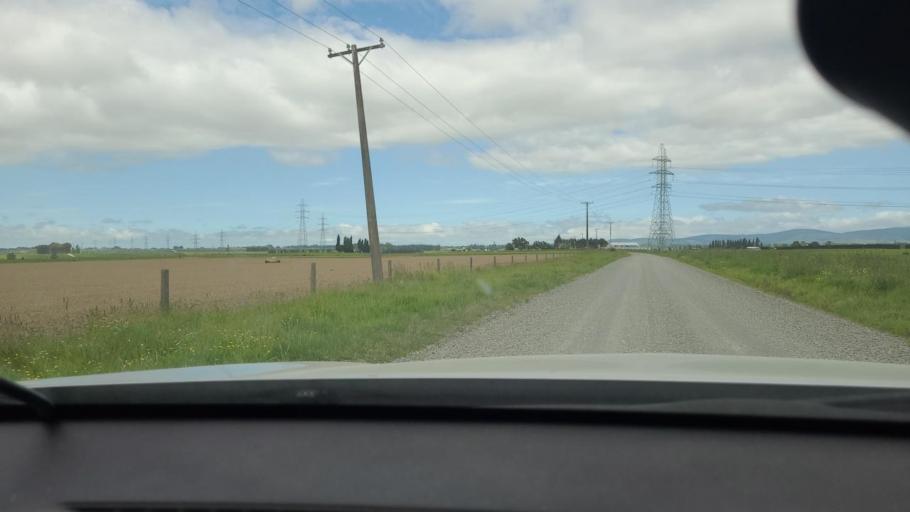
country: NZ
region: Southland
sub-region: Southland District
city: Winton
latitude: -46.0522
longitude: 168.0572
